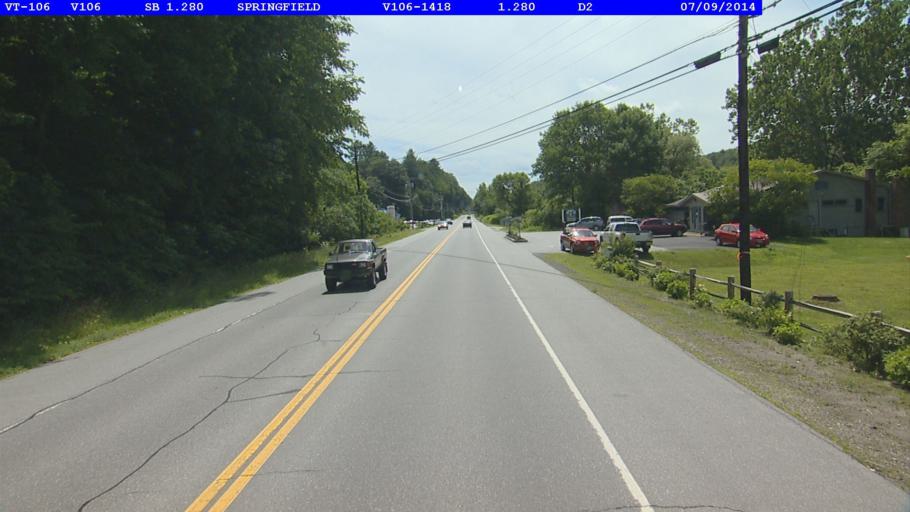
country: US
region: Vermont
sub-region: Windsor County
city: Springfield
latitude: 43.3193
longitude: -72.5053
